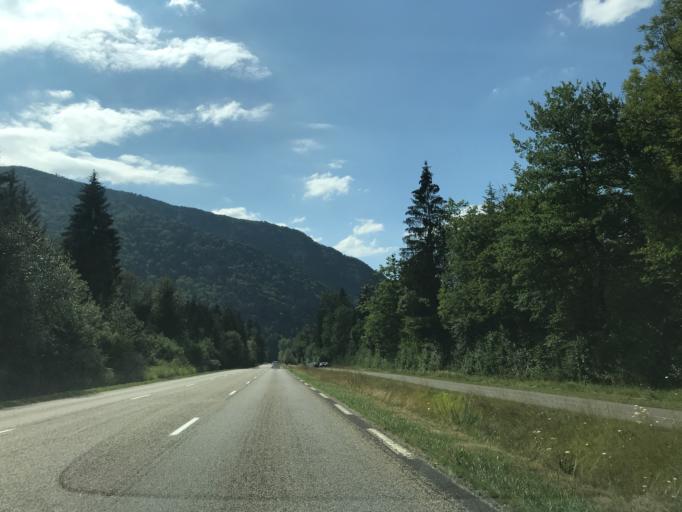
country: FR
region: Rhone-Alpes
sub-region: Departement de la Haute-Savoie
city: Dingy-Saint-Clair
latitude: 45.8968
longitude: 6.2265
